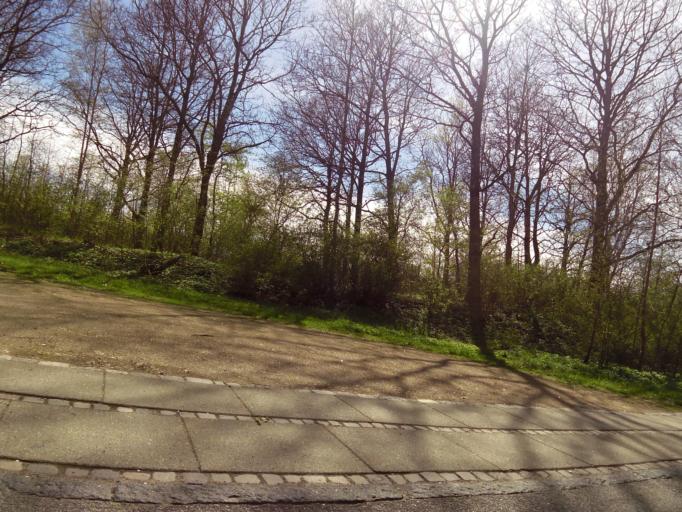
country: DK
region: Central Jutland
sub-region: Skive Kommune
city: Skive
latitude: 56.5676
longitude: 9.0094
